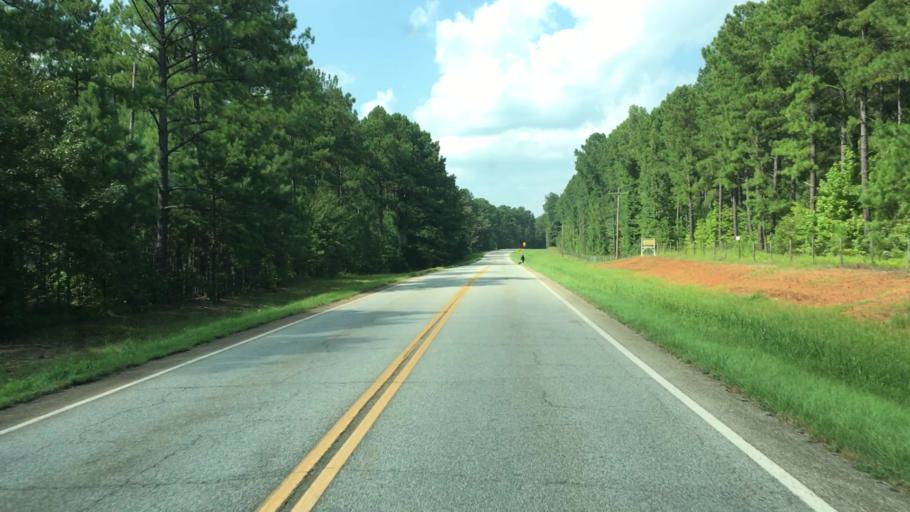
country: US
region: Georgia
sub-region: Monroe County
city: Forsyth
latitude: 33.1263
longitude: -83.8718
